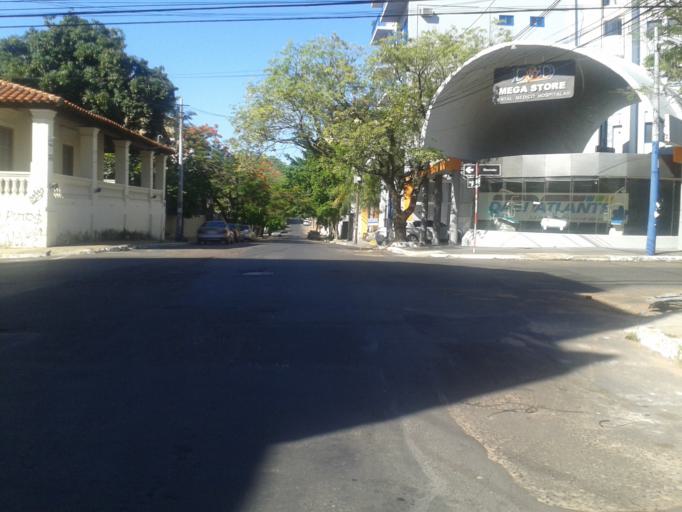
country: PY
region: Asuncion
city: Asuncion
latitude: -25.2871
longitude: -57.6410
